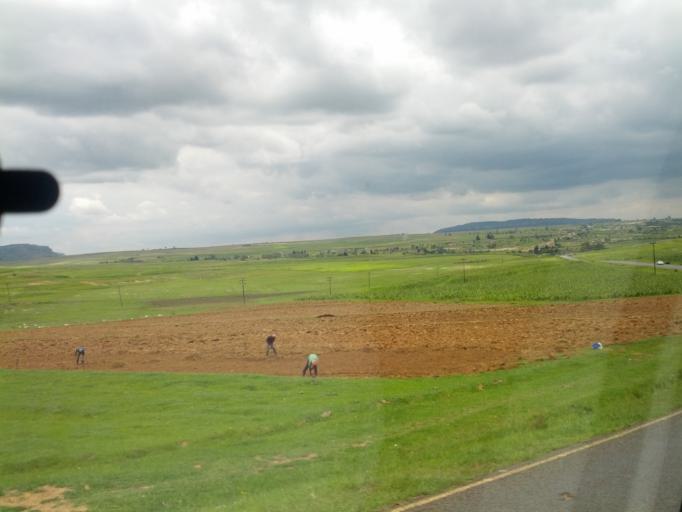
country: LS
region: Leribe
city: Leribe
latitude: -28.9221
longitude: 28.1281
